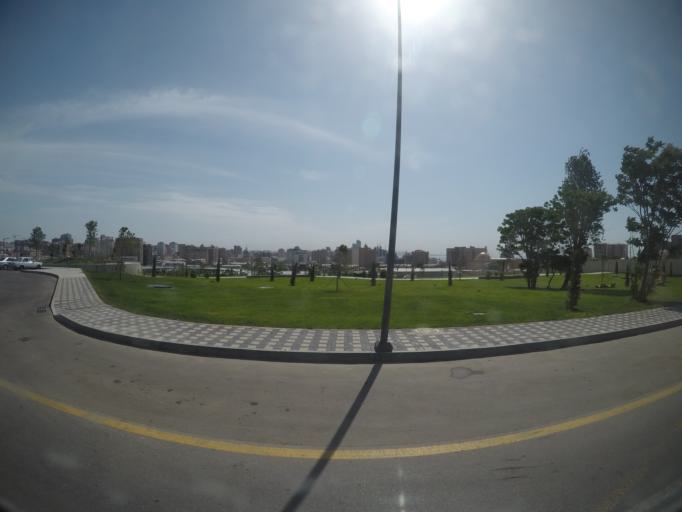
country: AZ
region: Baki
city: Badamdar
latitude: 40.3736
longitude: 49.8244
